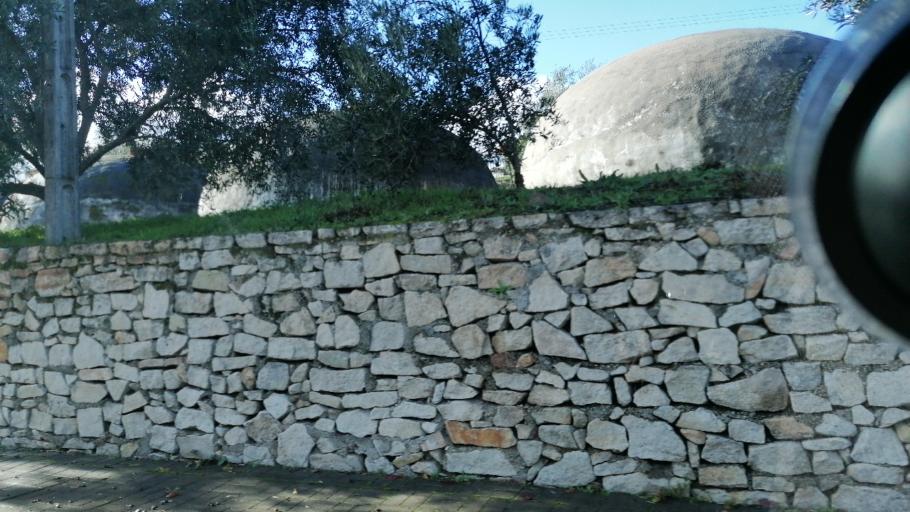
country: PT
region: Viseu
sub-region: Lamego
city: Lamego
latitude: 41.1039
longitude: -7.7951
